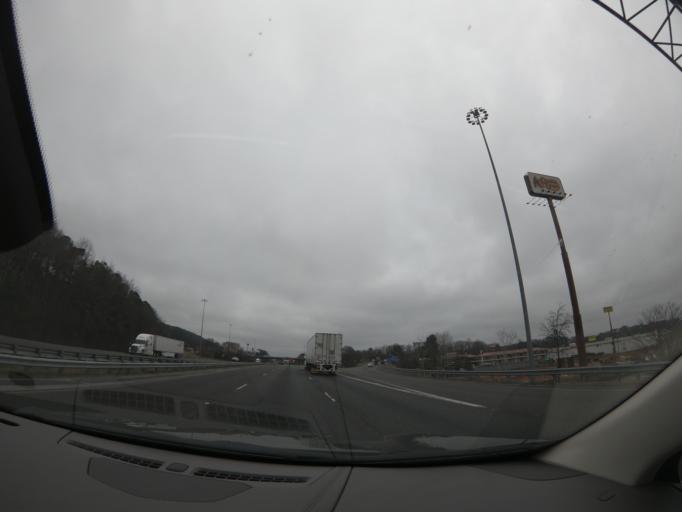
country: US
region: Georgia
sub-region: Whitfield County
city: Dalton
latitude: 34.7584
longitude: -85.0020
